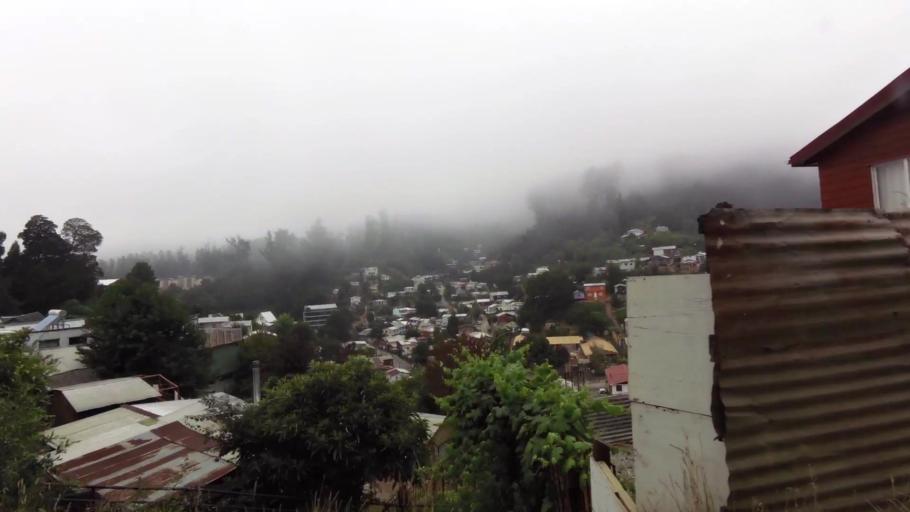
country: CL
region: Biobio
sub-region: Provincia de Concepcion
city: Concepcion
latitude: -36.8340
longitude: -73.0397
